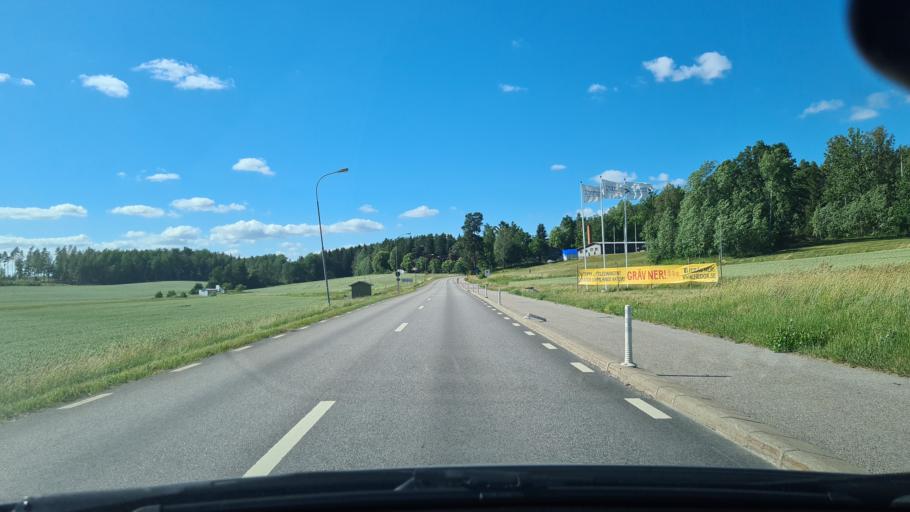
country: SE
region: Soedermanland
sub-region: Nykopings Kommun
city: Olstorp
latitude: 58.8315
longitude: 16.5176
